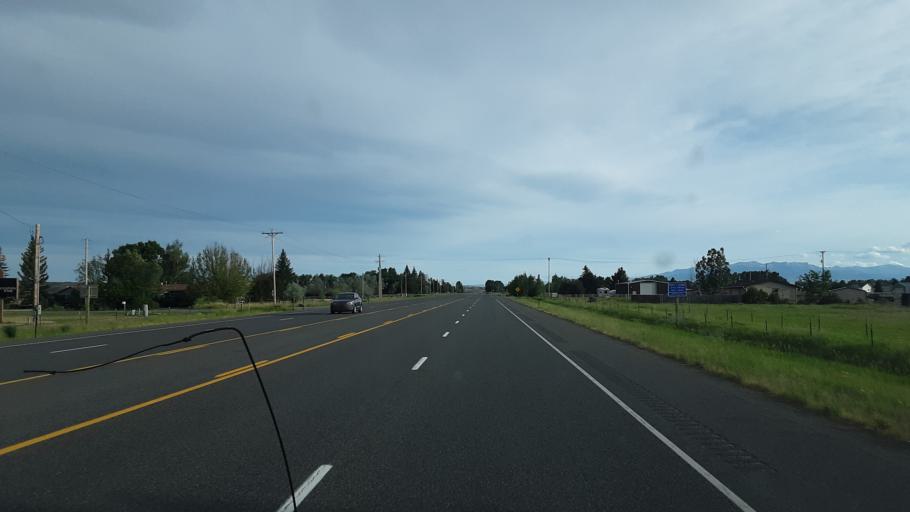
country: US
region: Wyoming
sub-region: Park County
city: Cody
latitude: 44.5989
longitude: -108.9654
